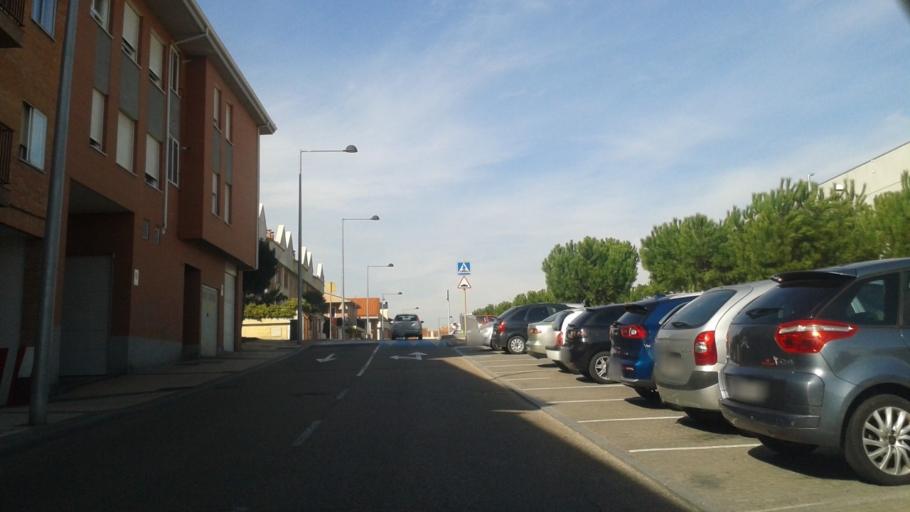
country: ES
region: Castille and Leon
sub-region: Provincia de Valladolid
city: Arroyo
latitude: 41.6267
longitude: -4.7683
